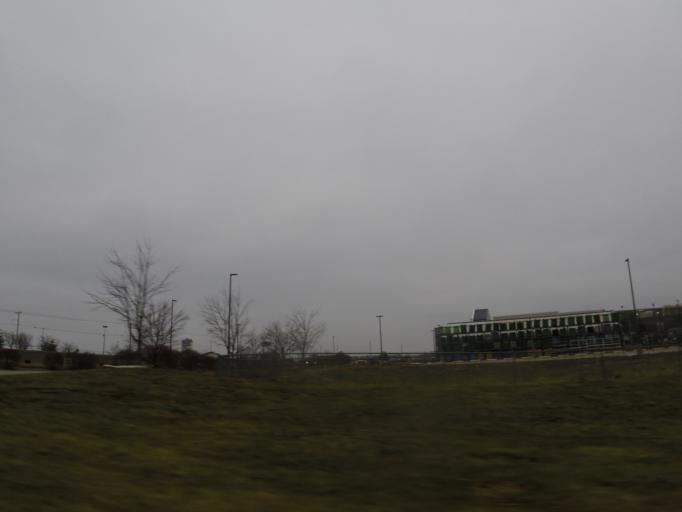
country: US
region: Missouri
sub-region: Marion County
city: Hannibal
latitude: 39.7213
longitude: -91.4010
